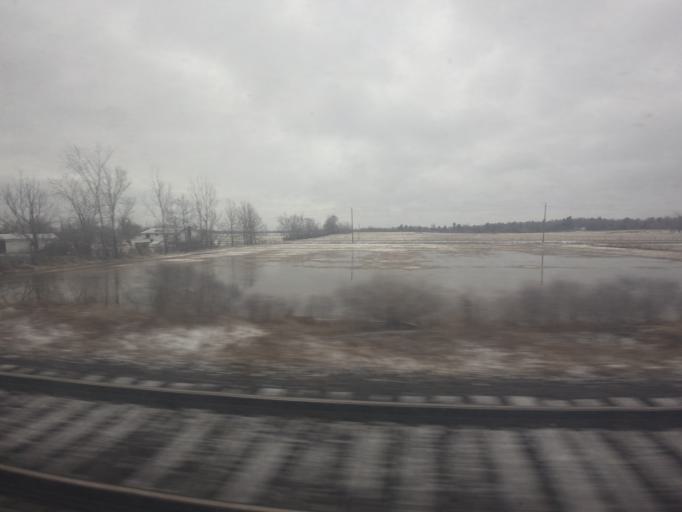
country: CA
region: Ontario
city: Gananoque
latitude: 44.3698
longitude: -76.1444
